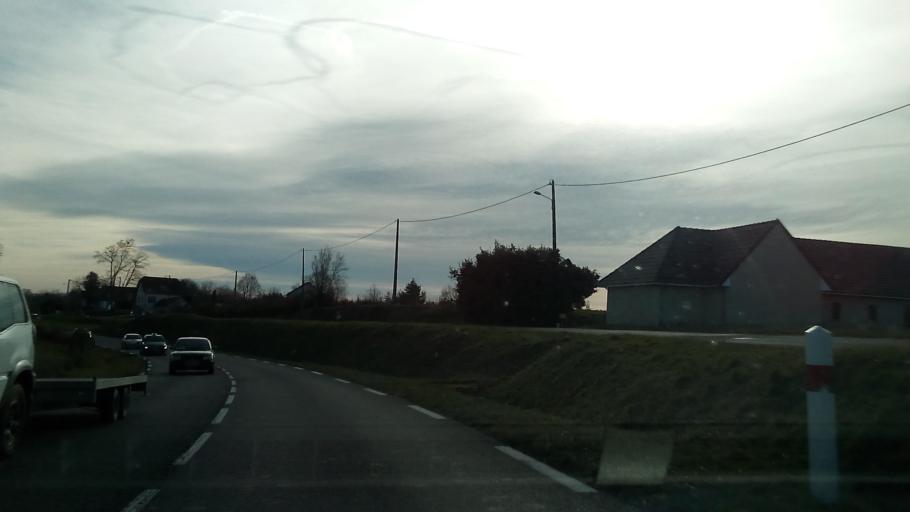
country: FR
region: Limousin
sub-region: Departement de la Correze
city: Seilhac
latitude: 45.3455
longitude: 1.7423
